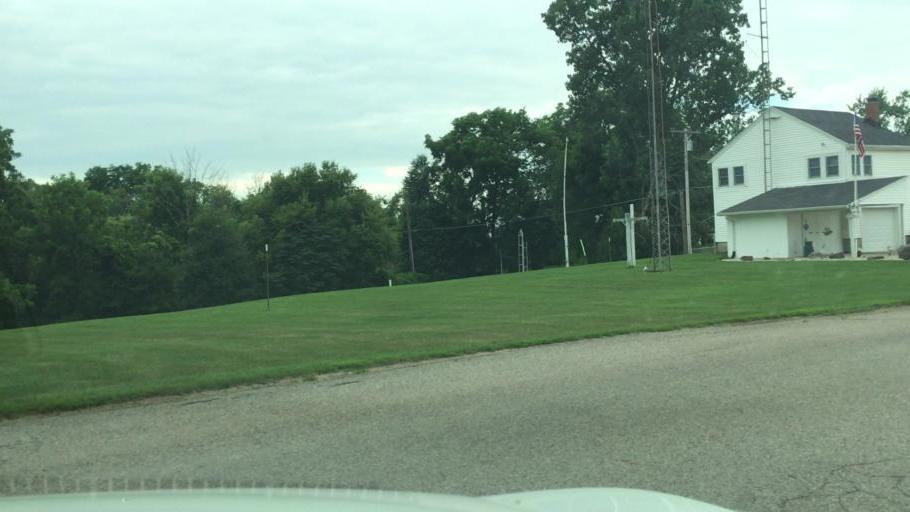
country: US
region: Ohio
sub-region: Champaign County
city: Mechanicsburg
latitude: 40.0742
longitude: -83.5667
